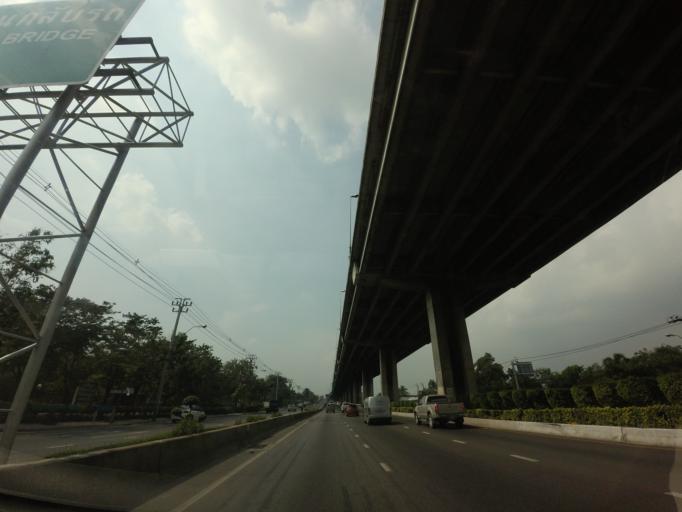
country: TH
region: Bangkok
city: Thawi Watthana
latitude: 13.7857
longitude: 100.3847
